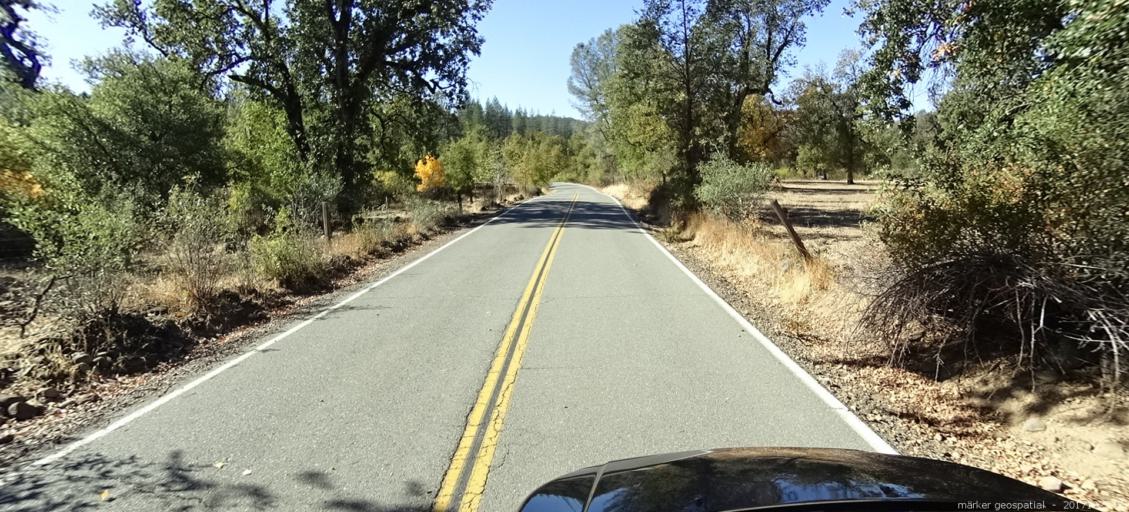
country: US
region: California
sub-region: Shasta County
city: Bella Vista
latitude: 40.7403
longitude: -121.9959
